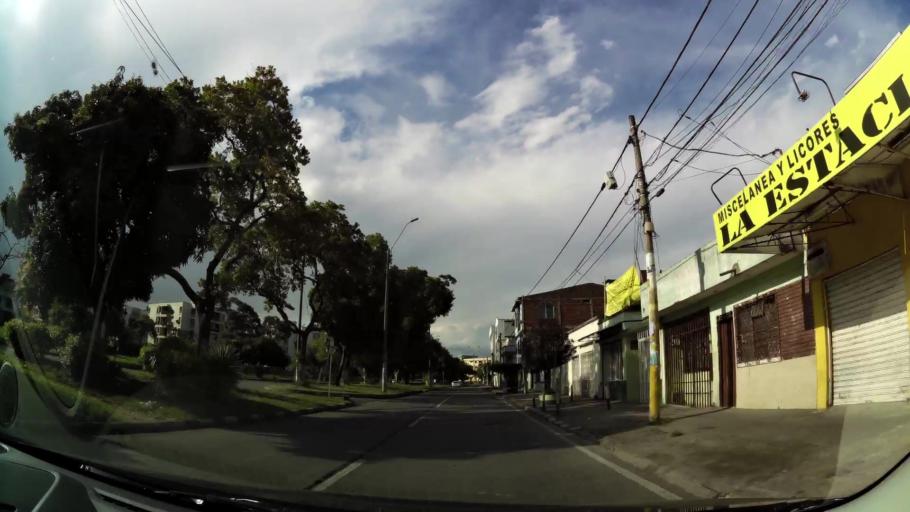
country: CO
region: Valle del Cauca
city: Cali
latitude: 3.4276
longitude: -76.5277
